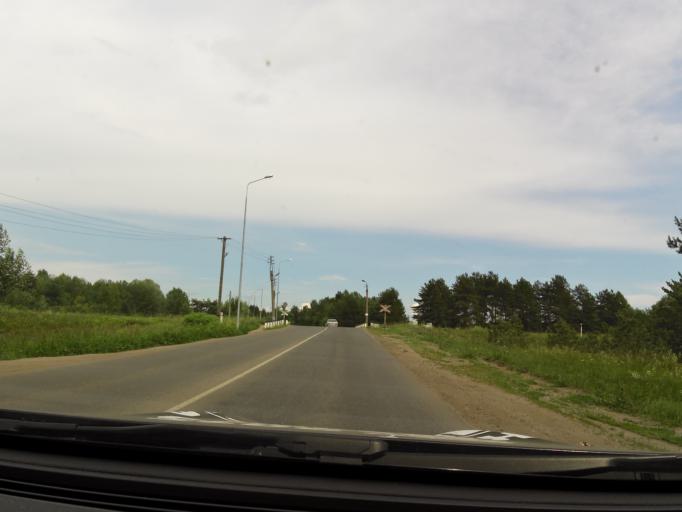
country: RU
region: Kirov
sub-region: Kirovo-Chepetskiy Rayon
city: Kirov
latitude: 58.6177
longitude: 49.7702
